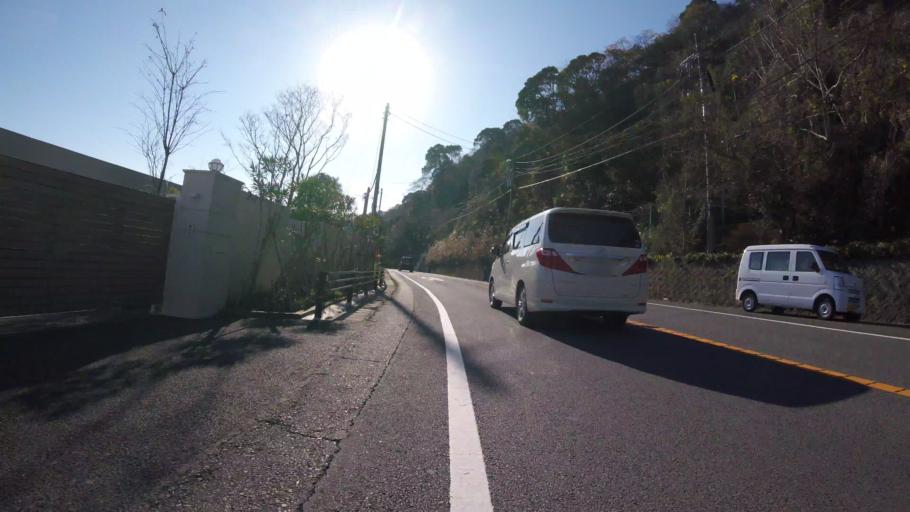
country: JP
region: Shizuoka
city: Atami
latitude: 35.0762
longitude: 139.0741
